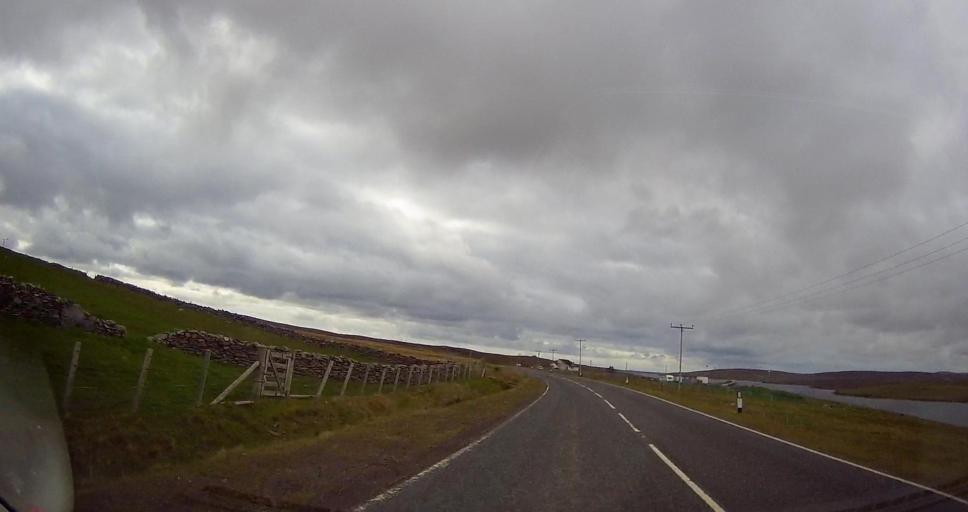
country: GB
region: Scotland
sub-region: Shetland Islands
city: Shetland
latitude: 60.6666
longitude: -1.0593
